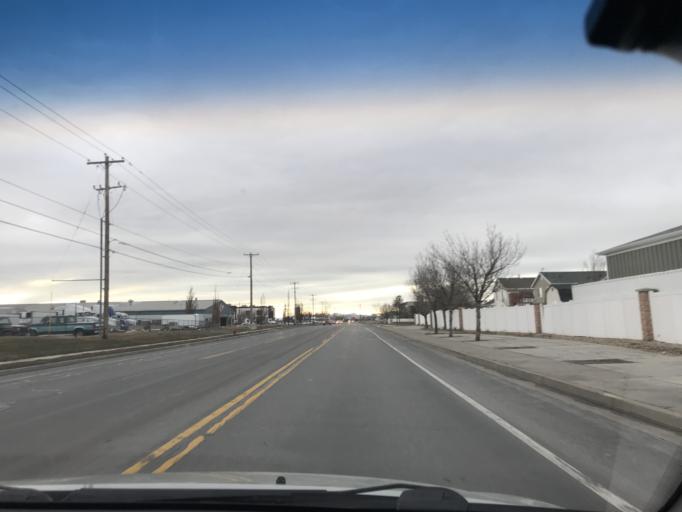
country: US
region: Utah
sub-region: Davis County
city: North Salt Lake
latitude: 40.8617
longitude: -111.9212
